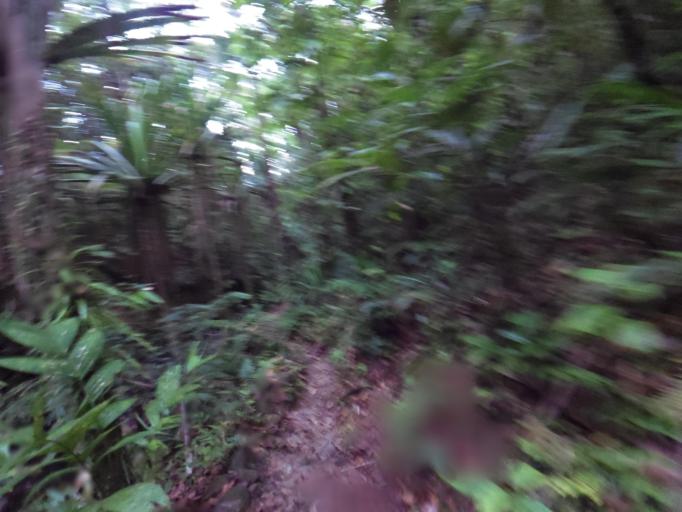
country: FJ
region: Central
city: Suva
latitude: -18.0591
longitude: 178.4688
